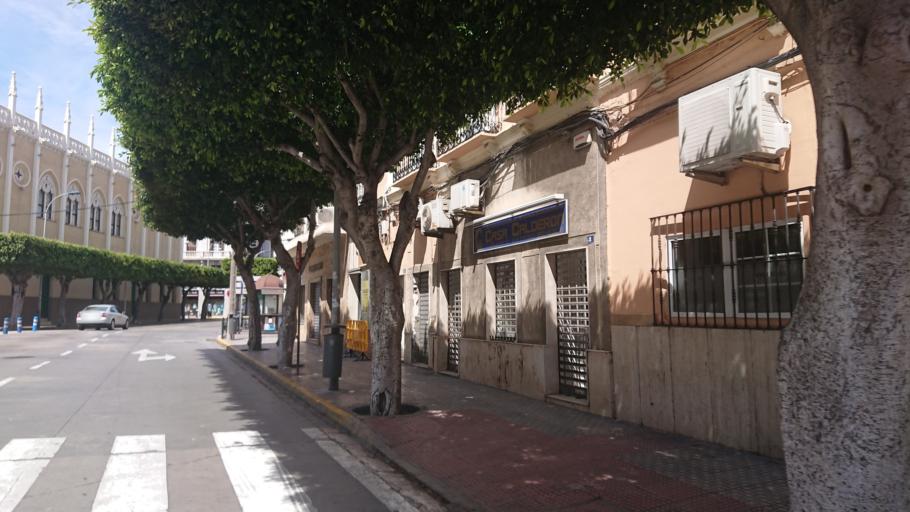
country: ES
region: Melilla
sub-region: Melilla
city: Melilla
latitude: 35.2934
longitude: -2.9428
